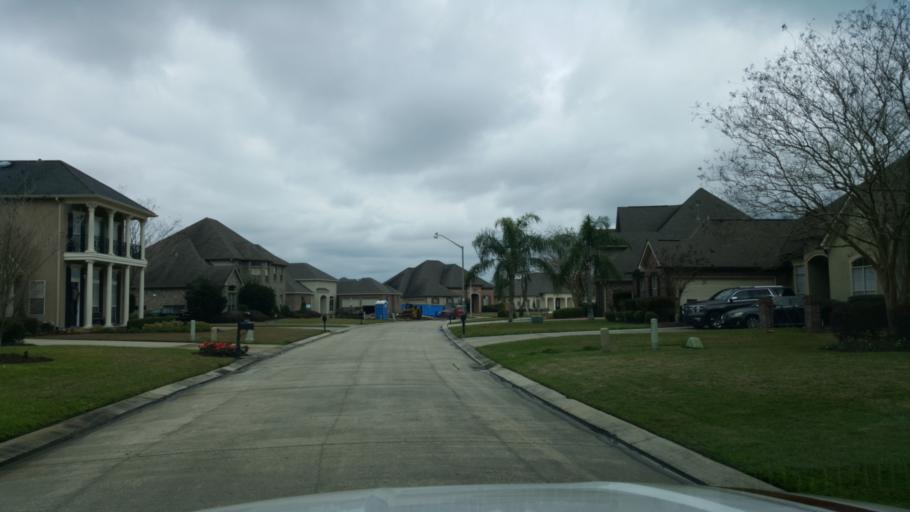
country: US
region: Louisiana
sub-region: Jefferson Parish
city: Woodmere
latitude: 29.8761
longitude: -90.0788
